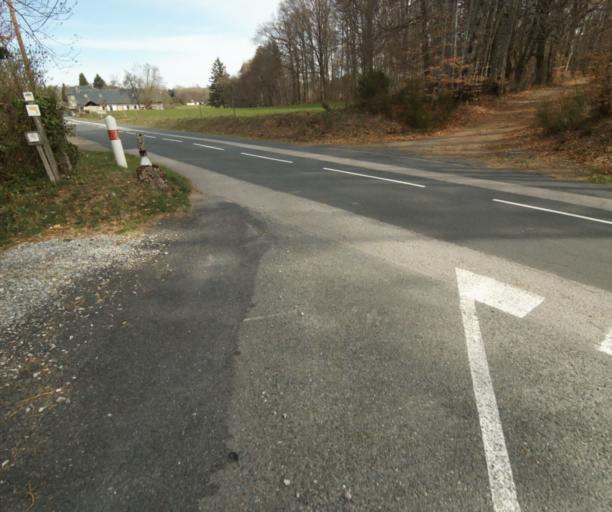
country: FR
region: Limousin
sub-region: Departement de la Correze
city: Correze
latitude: 45.4180
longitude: 1.8301
